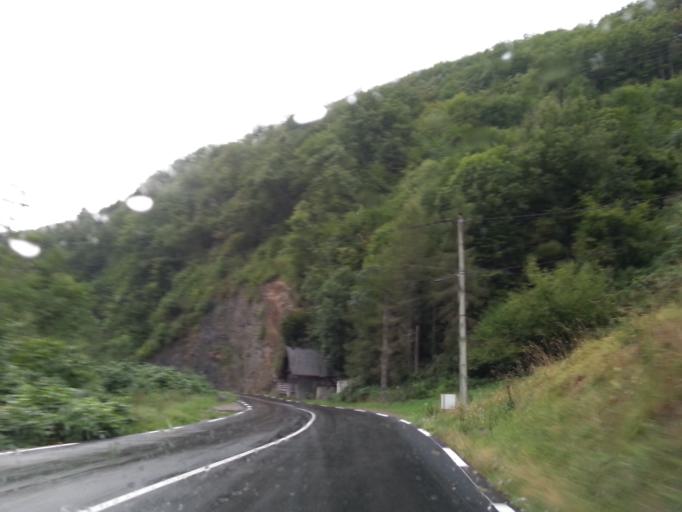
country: FR
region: Rhone-Alpes
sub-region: Departement de la Savoie
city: Marthod
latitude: 45.7138
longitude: 6.4429
